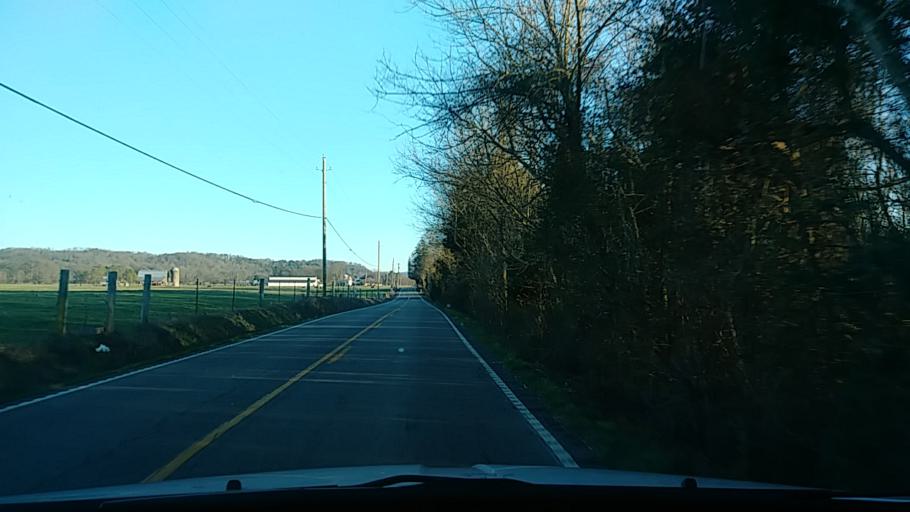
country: US
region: Tennessee
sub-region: Jefferson County
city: White Pine
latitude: 36.1412
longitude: -83.1420
